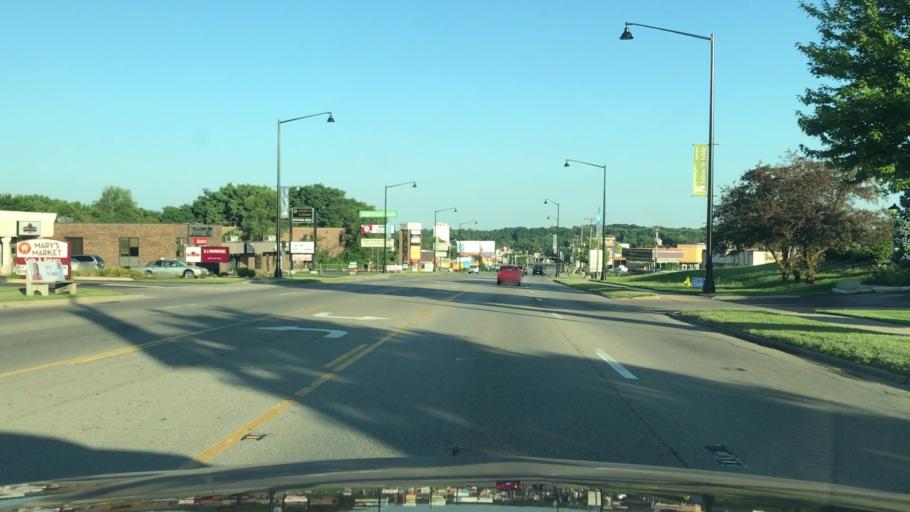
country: US
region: Illinois
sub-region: Winnebago County
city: Loves Park
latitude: 42.2643
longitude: -89.0305
